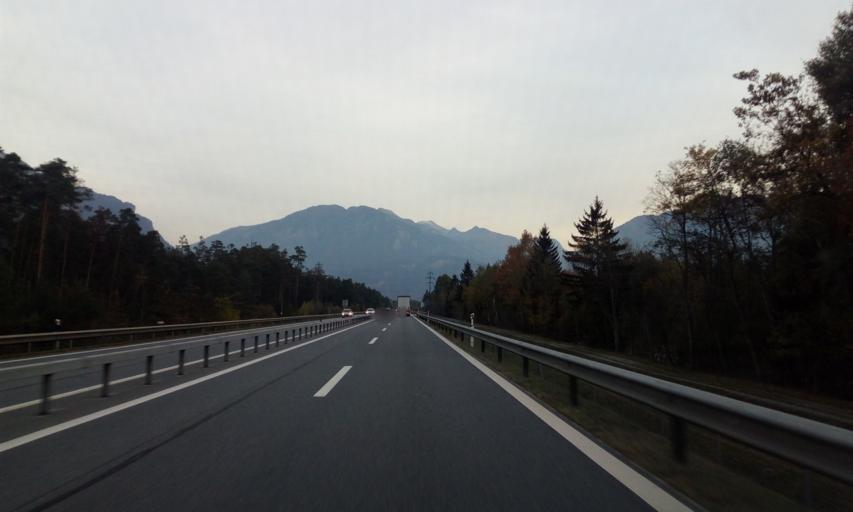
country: CH
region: Grisons
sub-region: Hinterrhein District
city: Cazis
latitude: 46.7516
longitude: 9.4284
